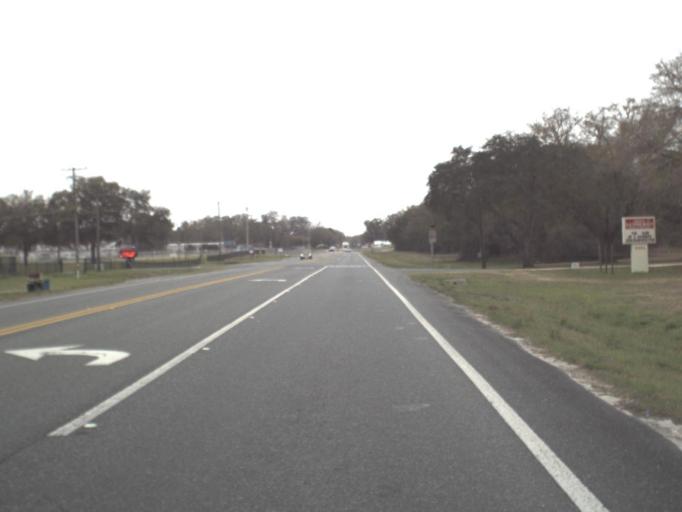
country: US
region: Florida
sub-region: Wakulla County
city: Crawfordville
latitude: 30.1094
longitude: -84.3773
